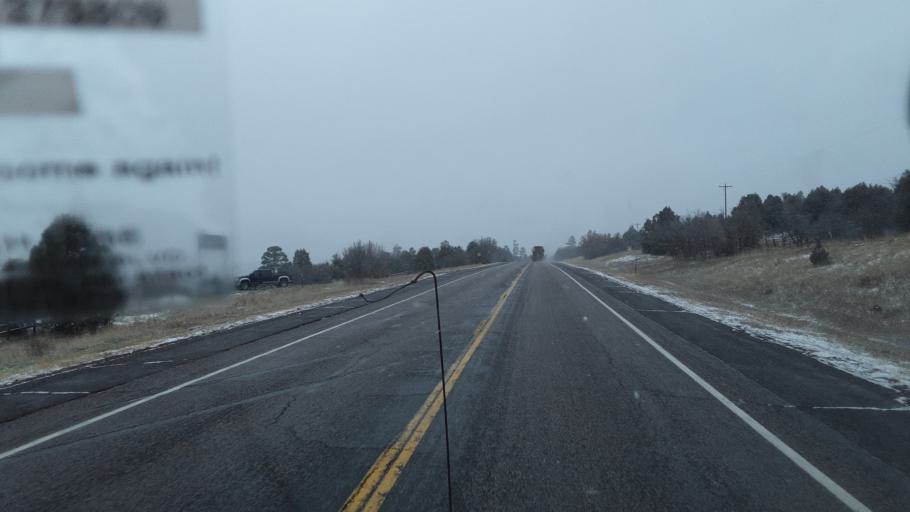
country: US
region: New Mexico
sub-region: Rio Arriba County
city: Tierra Amarilla
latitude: 36.7986
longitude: -106.5644
